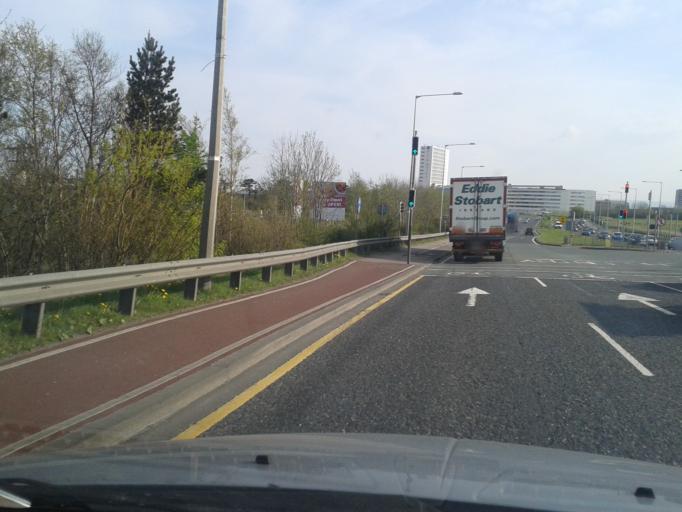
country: IE
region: Leinster
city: Ballymun
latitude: 53.4059
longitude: -6.2651
